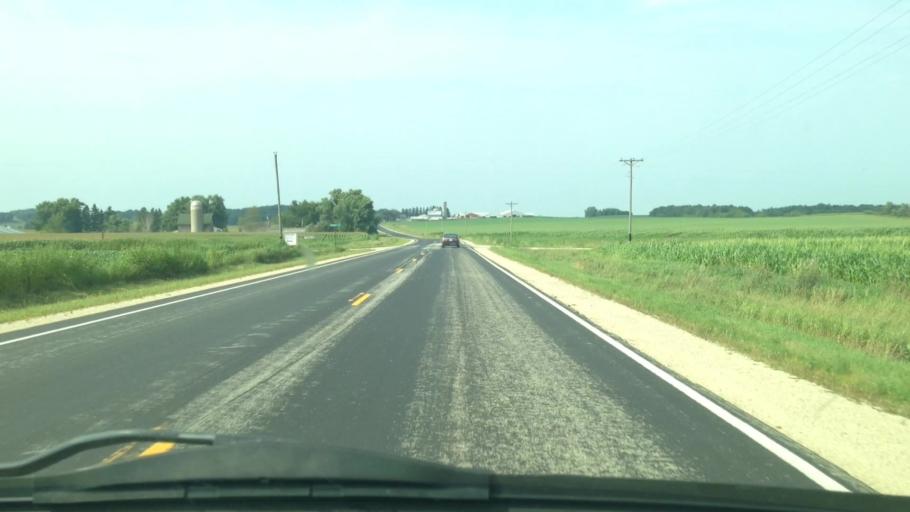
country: US
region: Minnesota
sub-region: Winona County
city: Lewiston
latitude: 43.9472
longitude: -91.9546
